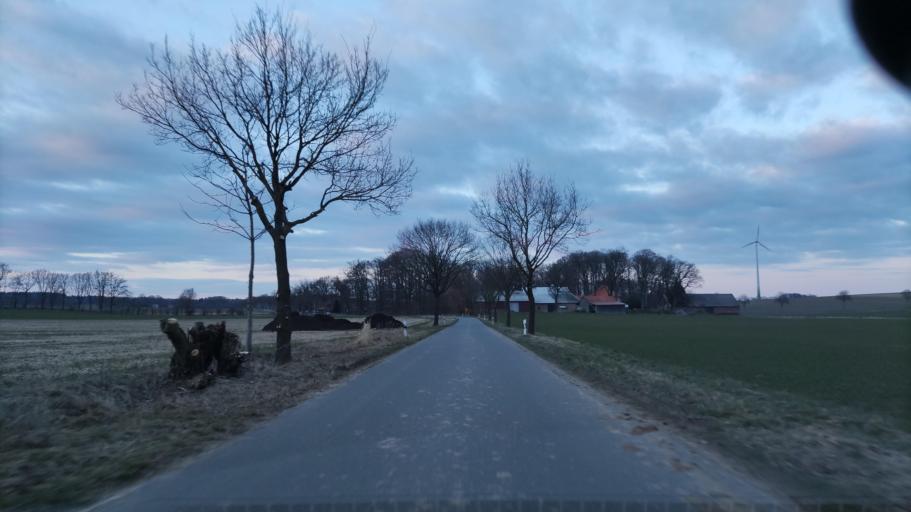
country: DE
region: Lower Saxony
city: Natendorf
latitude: 53.0812
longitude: 10.4449
